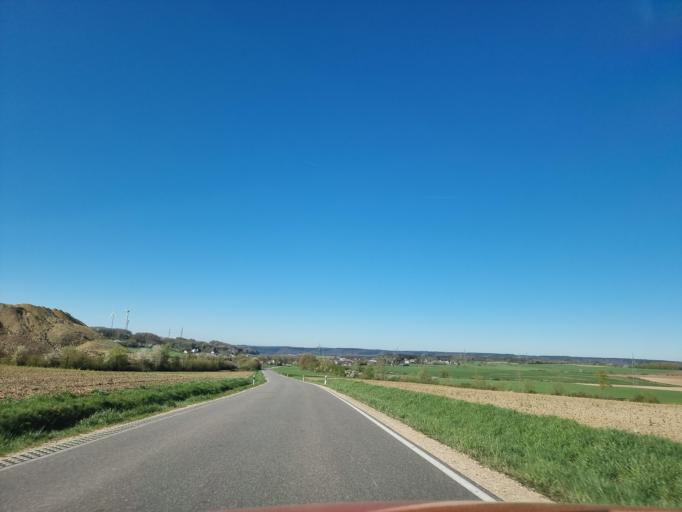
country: DE
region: Rheinland-Pfalz
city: Meckel
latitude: 49.8968
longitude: 6.5322
